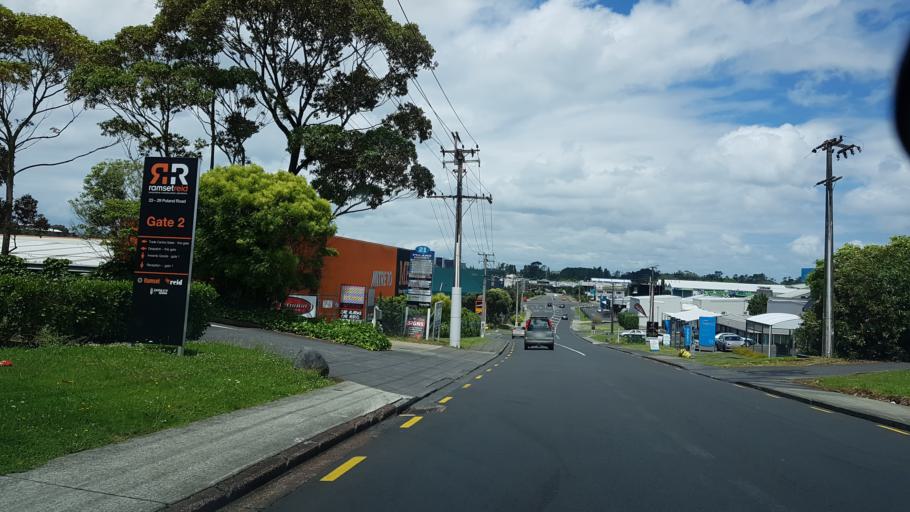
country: NZ
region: Auckland
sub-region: Auckland
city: North Shore
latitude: -36.7763
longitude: 174.7402
